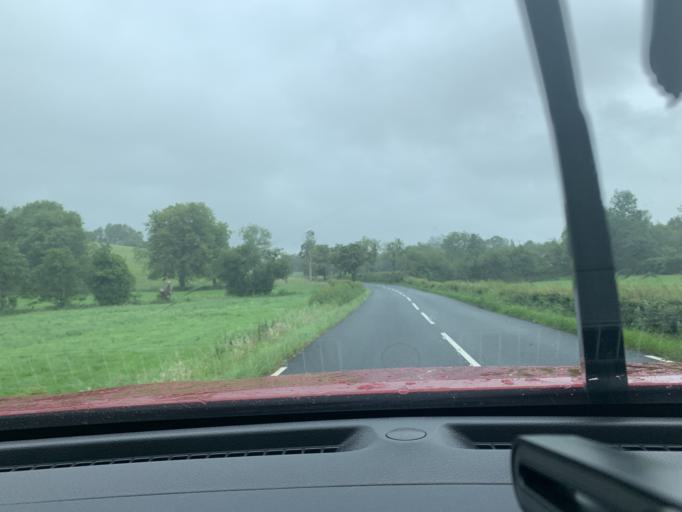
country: GB
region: Northern Ireland
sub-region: Fermanagh District
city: Enniskillen
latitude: 54.3036
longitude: -7.6893
